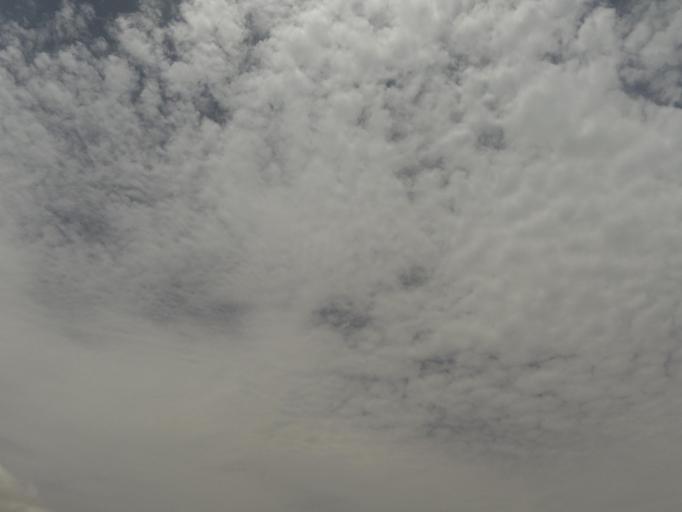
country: US
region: Florida
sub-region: Saint Johns County
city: Saint Augustine
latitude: 29.8968
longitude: -81.2757
